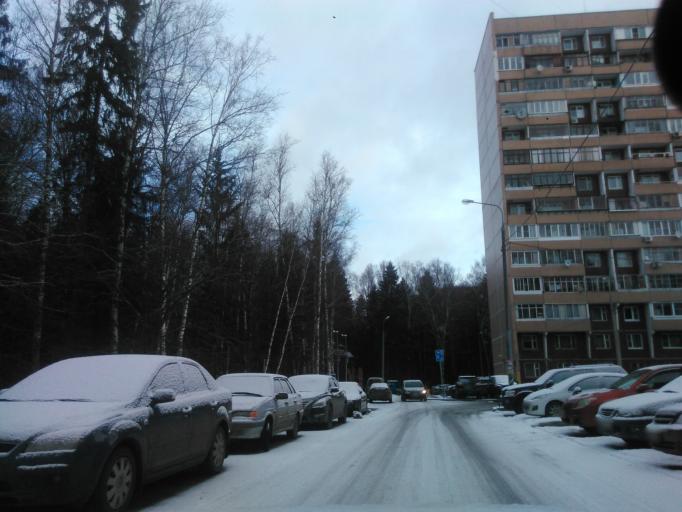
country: RU
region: Moscow
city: Zelenograd
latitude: 55.9959
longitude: 37.1742
